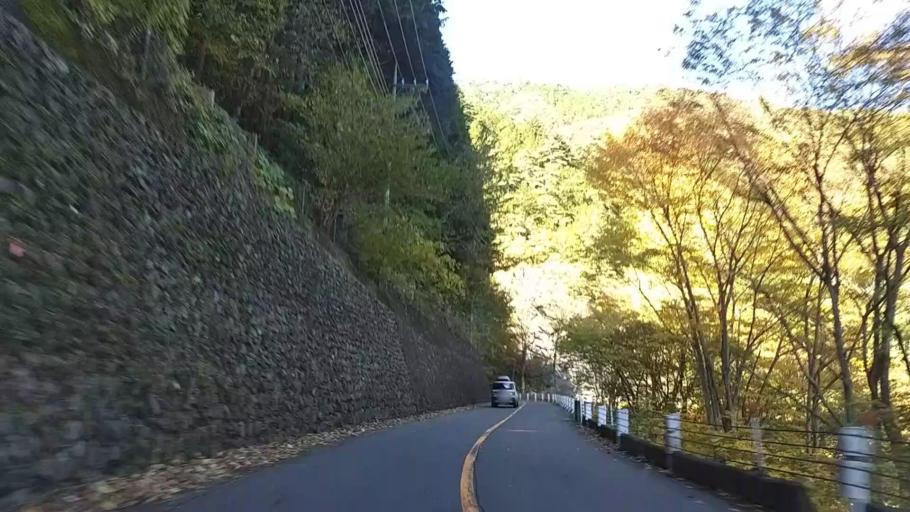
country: JP
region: Yamanashi
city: Otsuki
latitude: 35.7640
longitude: 138.9926
